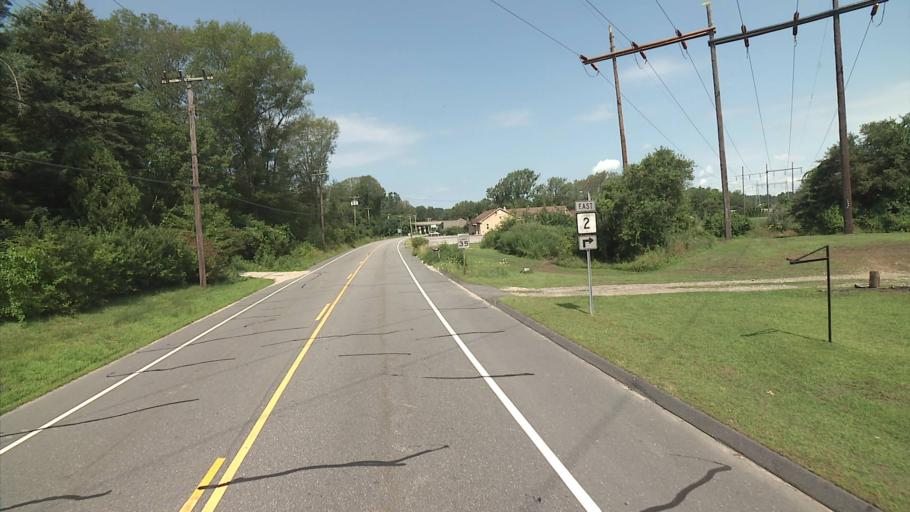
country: US
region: Connecticut
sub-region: New London County
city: Norwich
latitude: 41.5639
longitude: -72.1406
